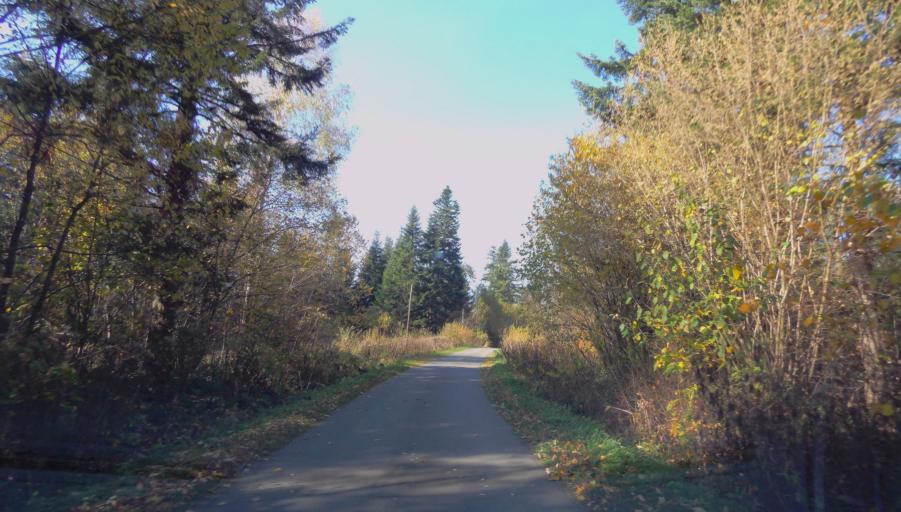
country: PL
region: Subcarpathian Voivodeship
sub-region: Powiat leski
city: Polanczyk
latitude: 49.3202
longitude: 22.4392
